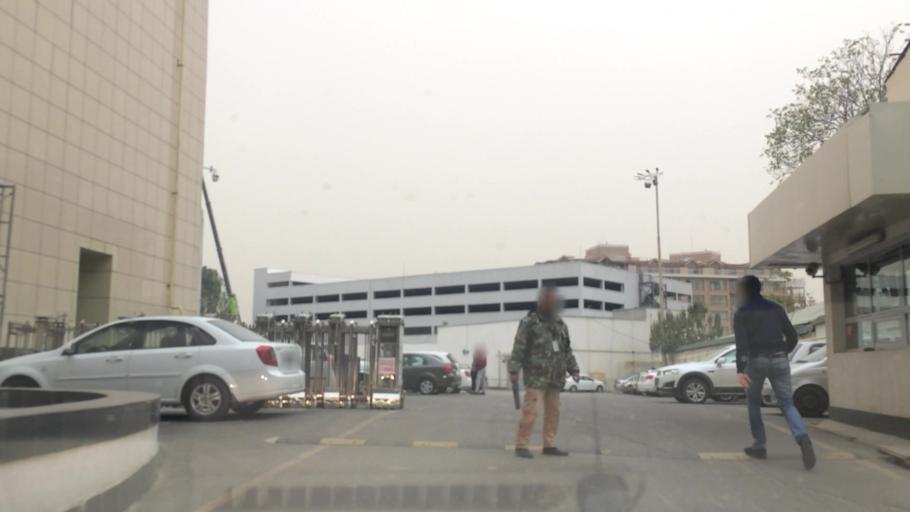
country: UZ
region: Toshkent Shahri
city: Tashkent
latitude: 41.2987
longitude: 69.2492
